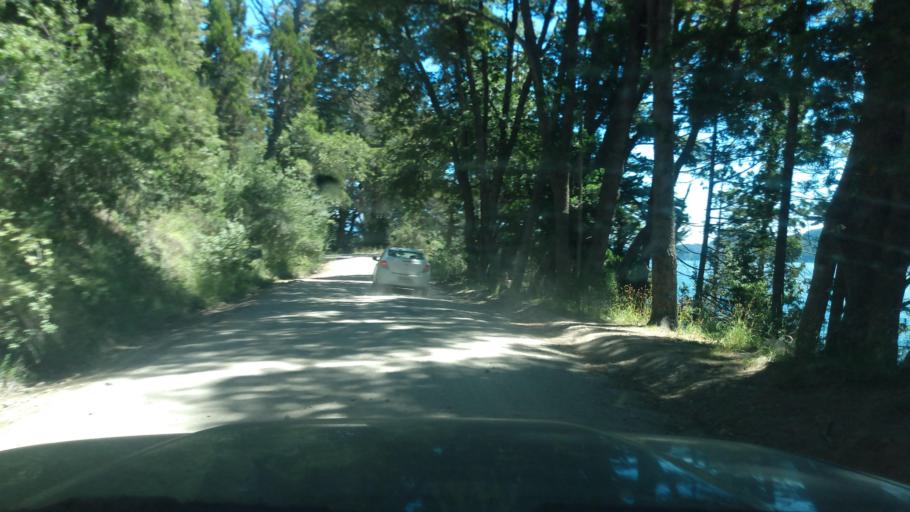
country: AR
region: Rio Negro
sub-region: Departamento de Bariloche
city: San Carlos de Bariloche
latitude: -41.1105
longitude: -71.4756
